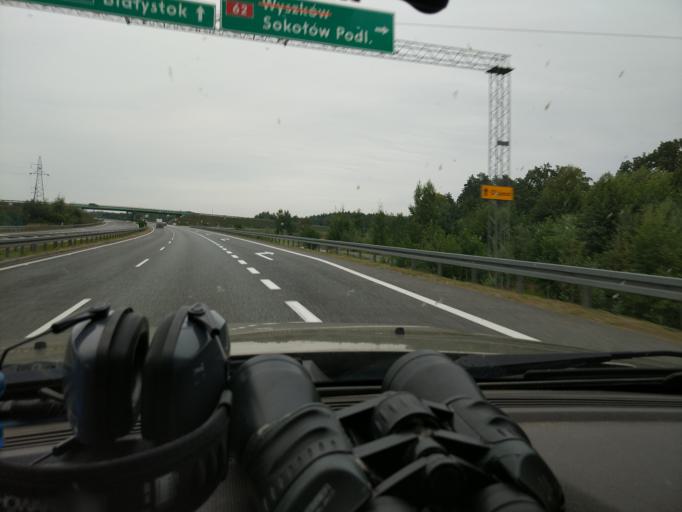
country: PL
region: Masovian Voivodeship
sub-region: Powiat wyszkowski
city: Wyszkow
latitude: 52.5853
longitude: 21.4984
